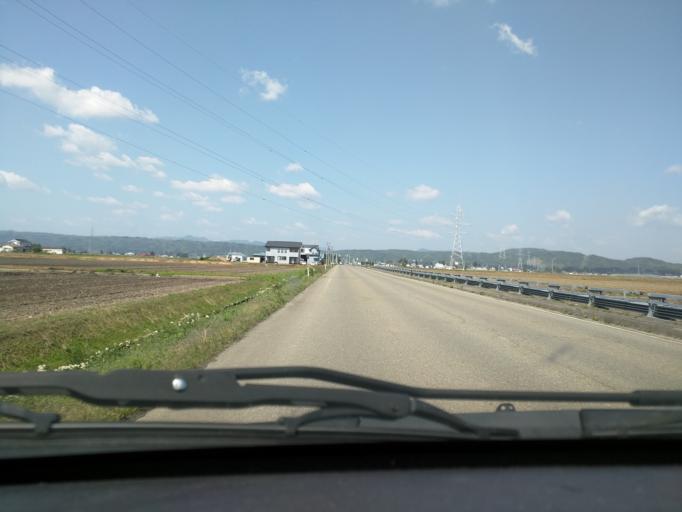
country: JP
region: Fukushima
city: Kitakata
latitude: 37.5804
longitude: 139.8512
